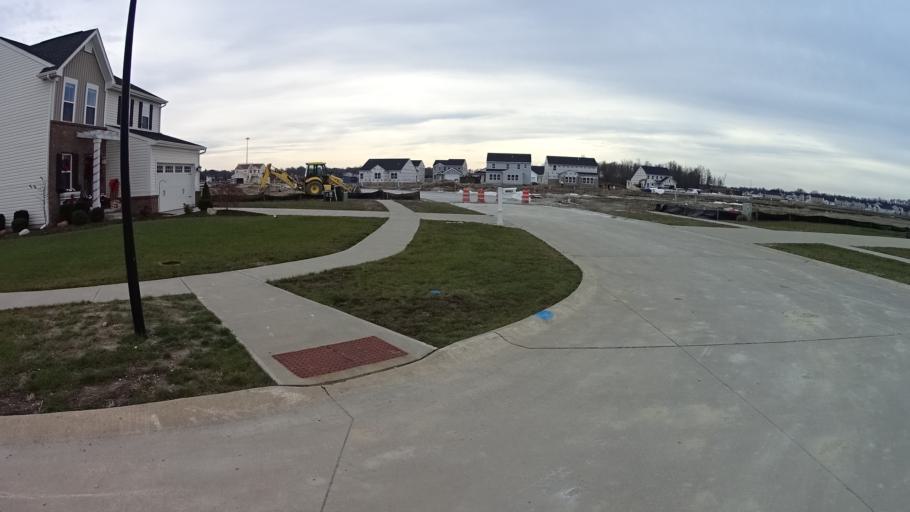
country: US
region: Ohio
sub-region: Lorain County
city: North Ridgeville
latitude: 41.3967
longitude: -82.0319
